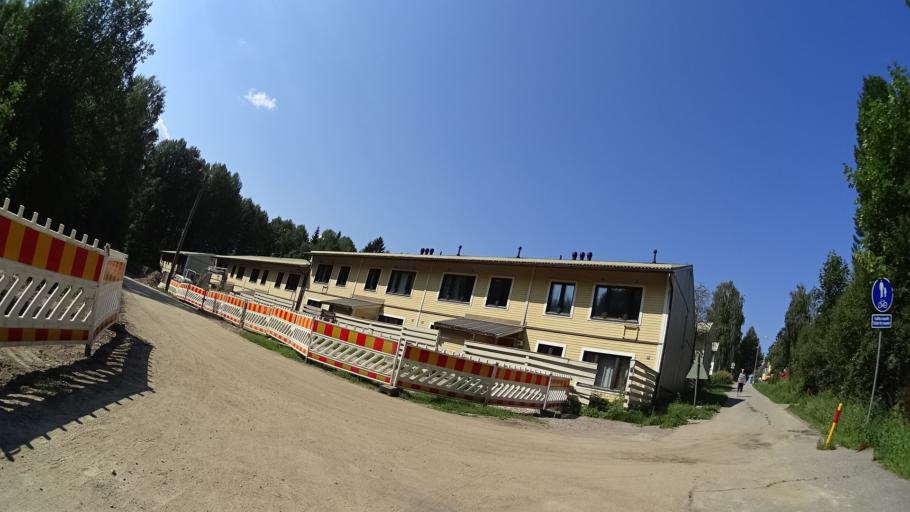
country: FI
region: Uusimaa
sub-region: Helsinki
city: Vantaa
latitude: 60.3440
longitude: 25.0697
